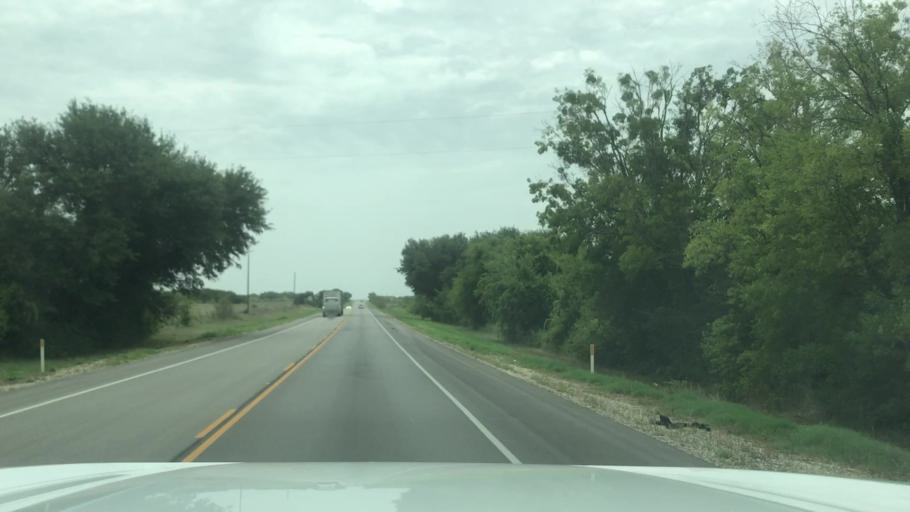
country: US
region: Texas
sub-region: Erath County
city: Dublin
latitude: 32.0841
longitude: -98.2509
